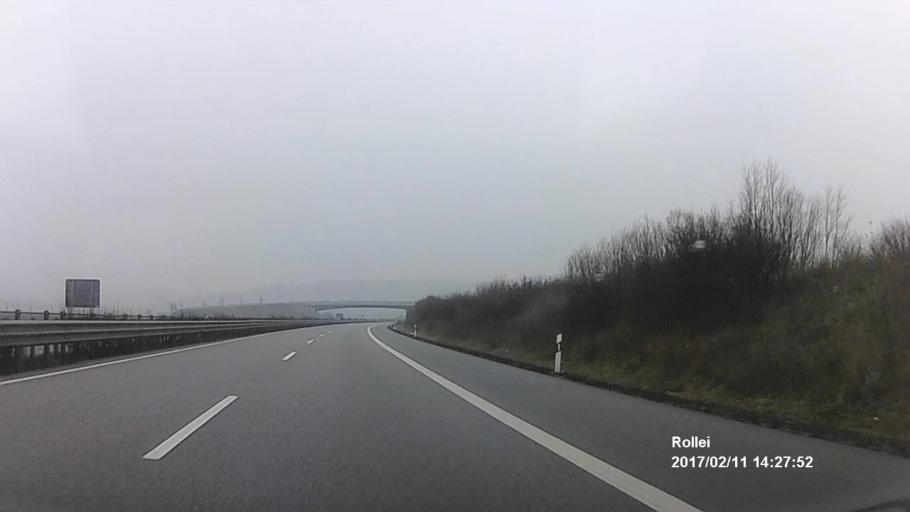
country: DE
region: Thuringia
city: Oberheldrungen
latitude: 51.2956
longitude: 11.2363
